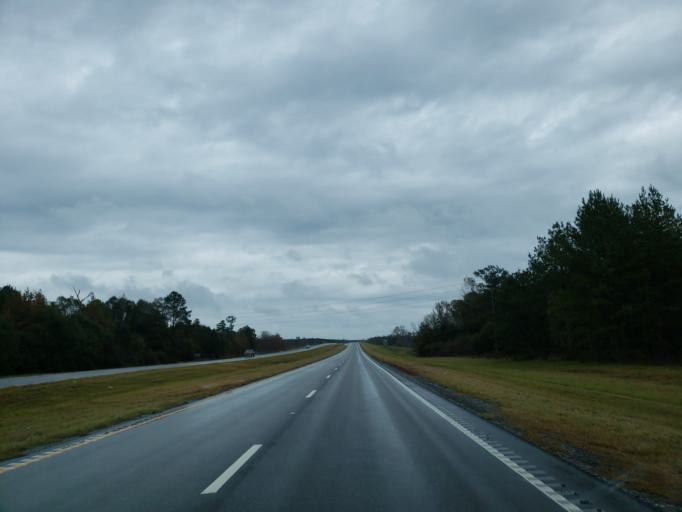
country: US
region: Mississippi
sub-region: Wayne County
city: Waynesboro
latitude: 31.6880
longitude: -88.6696
